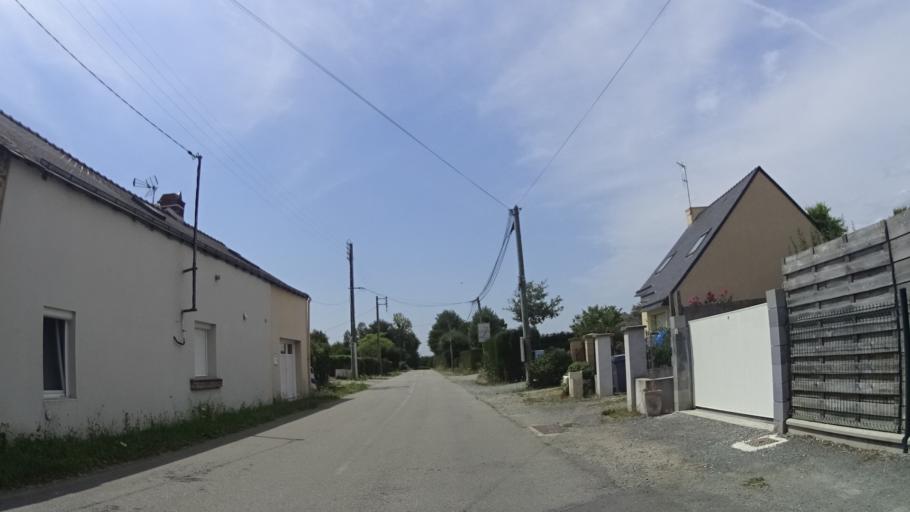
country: FR
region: Pays de la Loire
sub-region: Departement de la Loire-Atlantique
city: Fay-de-Bretagne
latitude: 47.4044
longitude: -1.7967
